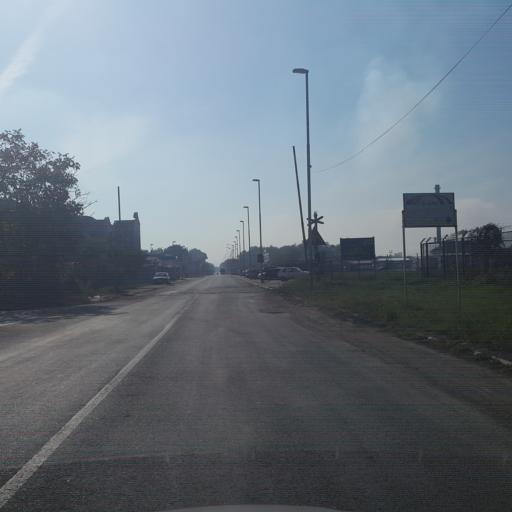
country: RS
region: Central Serbia
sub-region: Pirotski Okrug
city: Pirot
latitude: 43.1797
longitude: 22.5765
